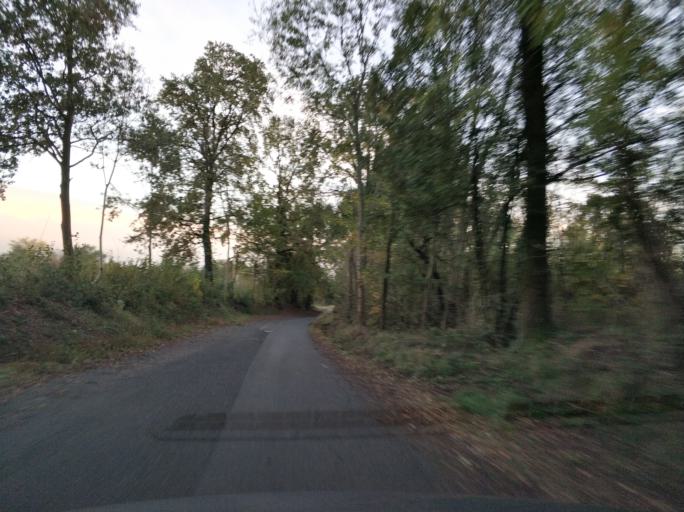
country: IT
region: Piedmont
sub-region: Provincia di Torino
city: Robassomero
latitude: 45.1905
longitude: 7.5787
